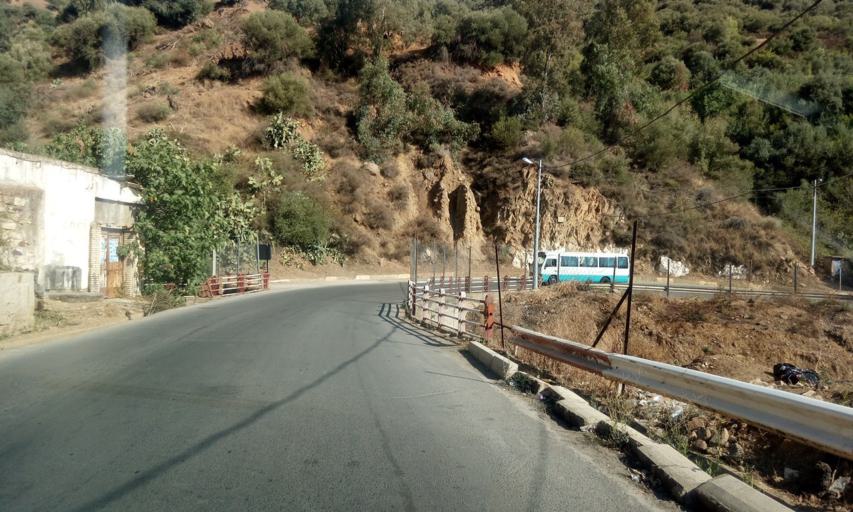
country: DZ
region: Tizi Ouzou
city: Chemini
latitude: 36.6066
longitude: 4.6395
